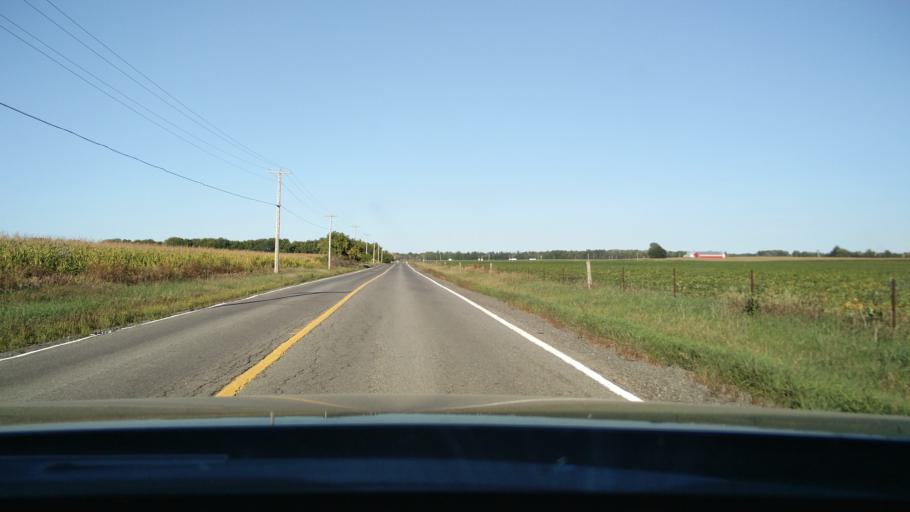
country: CA
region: Ontario
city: Bells Corners
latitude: 45.2098
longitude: -75.7911
